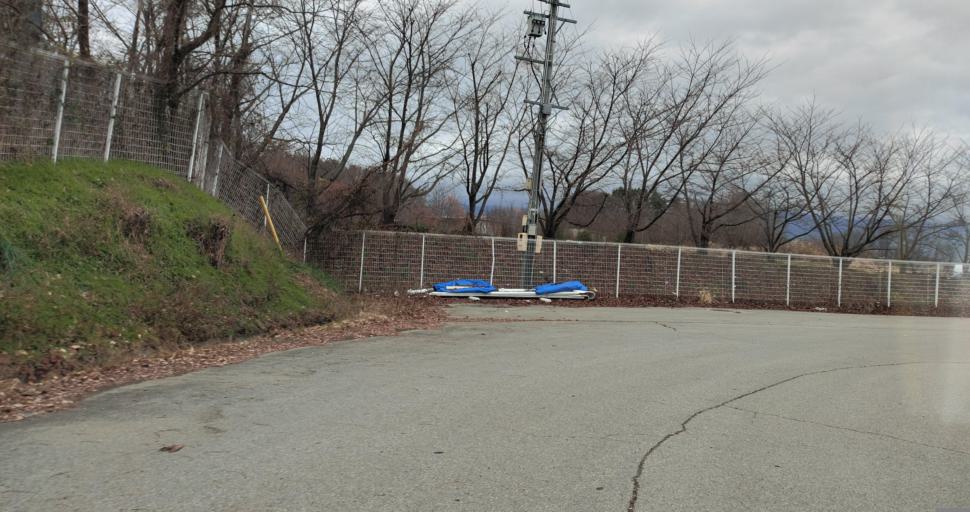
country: JP
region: Nagano
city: Komoro
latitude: 36.2868
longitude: 138.4897
